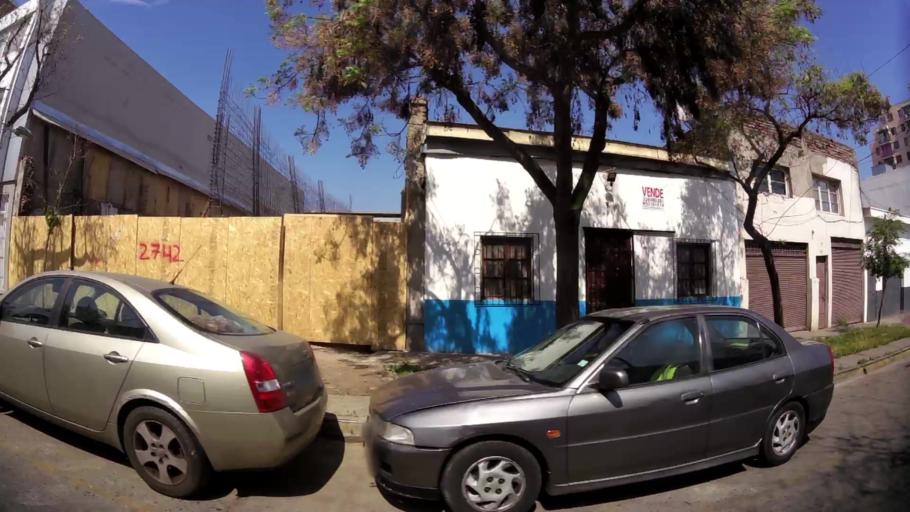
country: CL
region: Santiago Metropolitan
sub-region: Provincia de Santiago
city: Santiago
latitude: -33.4559
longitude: -70.6735
